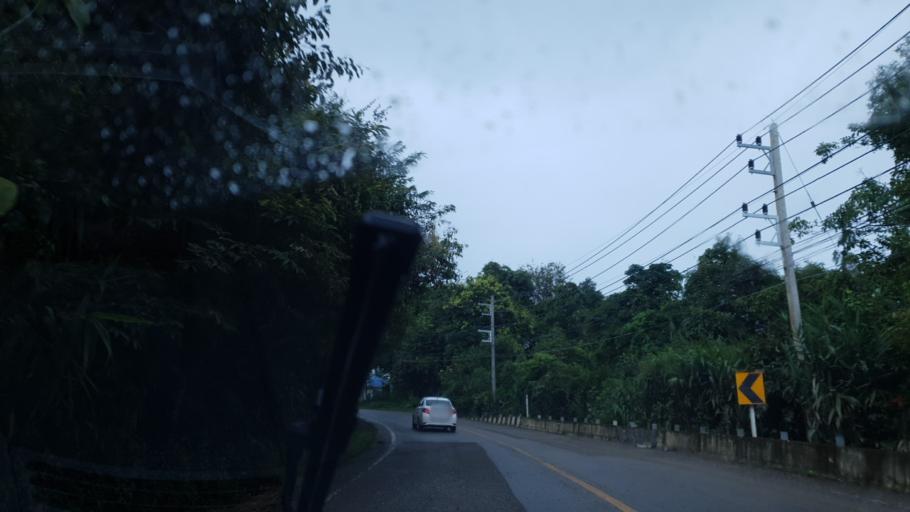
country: TH
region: Mae Hong Son
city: Ban Huai I Huak
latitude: 18.1508
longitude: 98.1281
